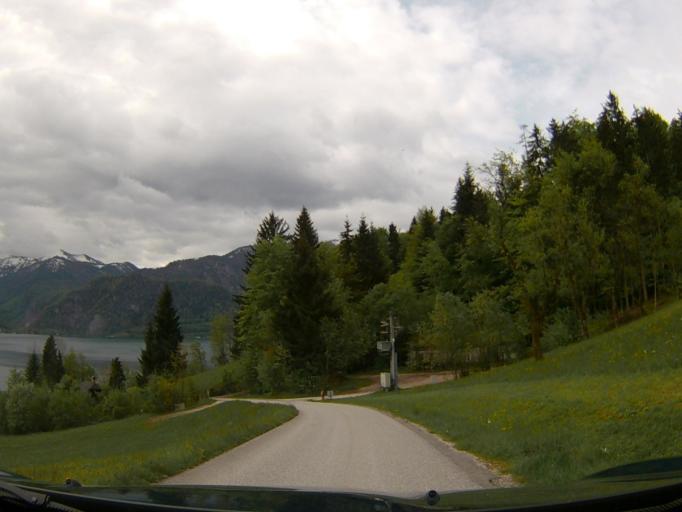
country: AT
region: Upper Austria
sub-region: Politischer Bezirk Vocklabruck
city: Steinbach am Attersee
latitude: 47.8235
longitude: 13.5079
